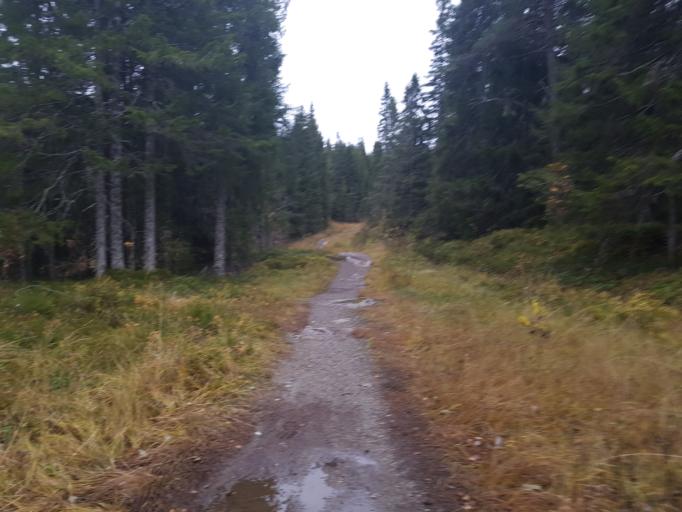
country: NO
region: Sor-Trondelag
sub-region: Melhus
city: Melhus
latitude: 63.3827
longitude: 10.2499
